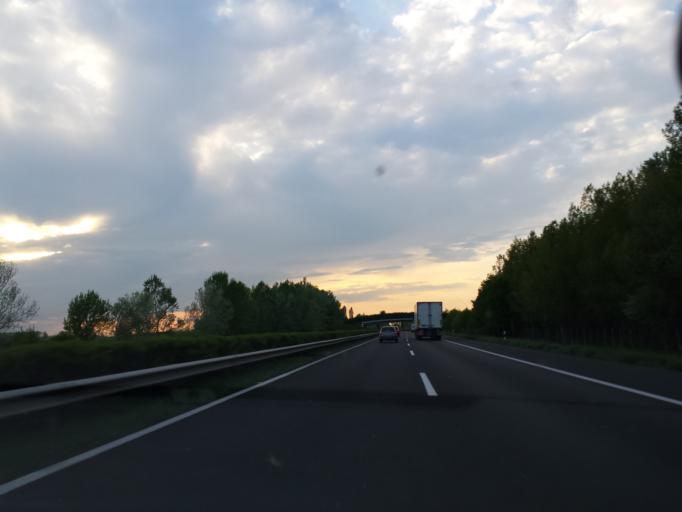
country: HU
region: Gyor-Moson-Sopron
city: Kimle
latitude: 47.7975
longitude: 17.3131
